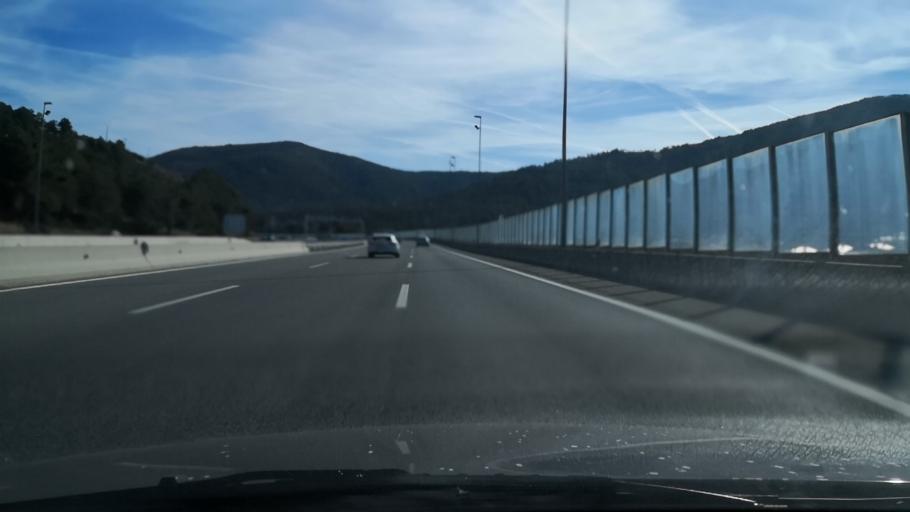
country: ES
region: Castille and Leon
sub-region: Provincia de Avila
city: Peguerinos
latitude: 40.7186
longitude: -4.1889
